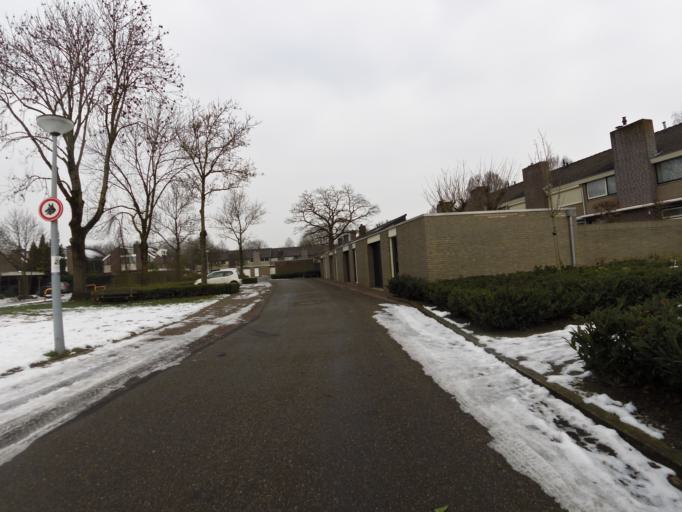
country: NL
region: Gelderland
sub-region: Gemeente Zevenaar
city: Zevenaar
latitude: 51.9368
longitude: 6.0655
